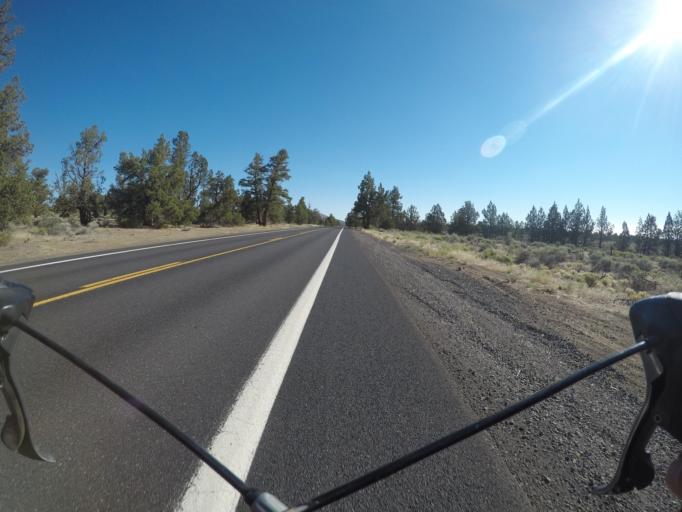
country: US
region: Oregon
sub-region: Deschutes County
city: Redmond
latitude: 44.2166
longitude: -121.3144
